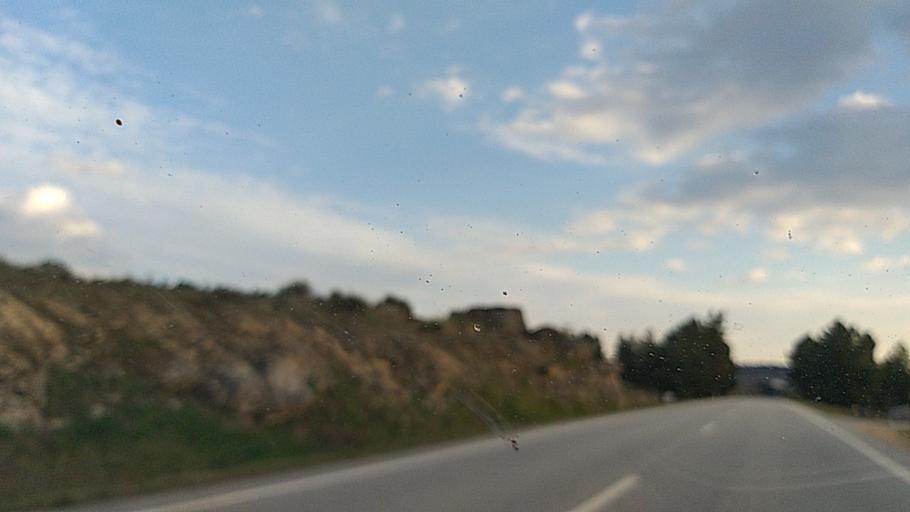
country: PT
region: Guarda
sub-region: Pinhel
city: Pinhel
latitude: 40.6796
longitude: -6.9503
